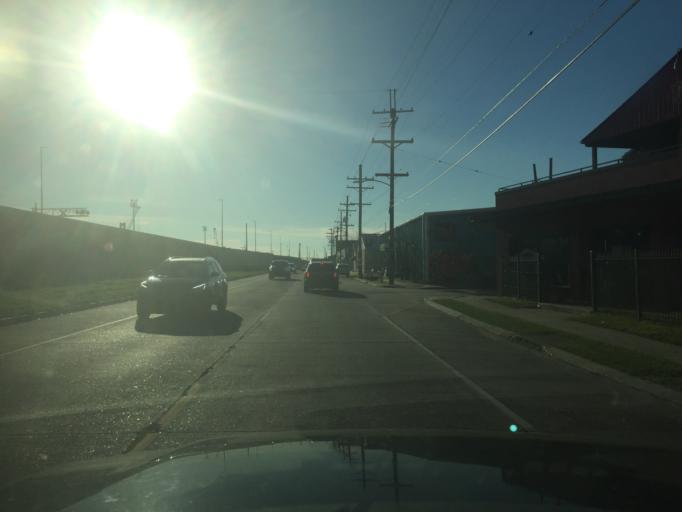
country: US
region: Louisiana
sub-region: Jefferson Parish
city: Harvey
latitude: 29.9197
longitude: -90.0814
